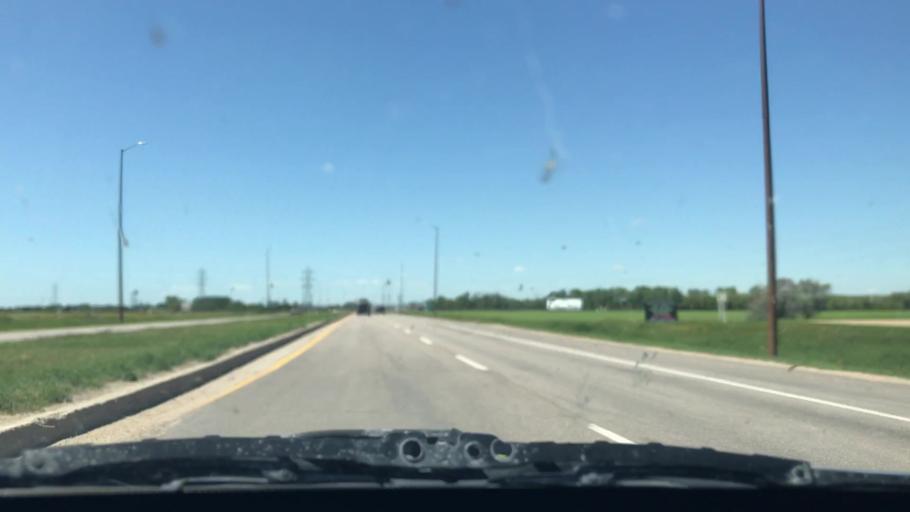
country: CA
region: Manitoba
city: Winnipeg
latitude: 49.8388
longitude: -96.9805
